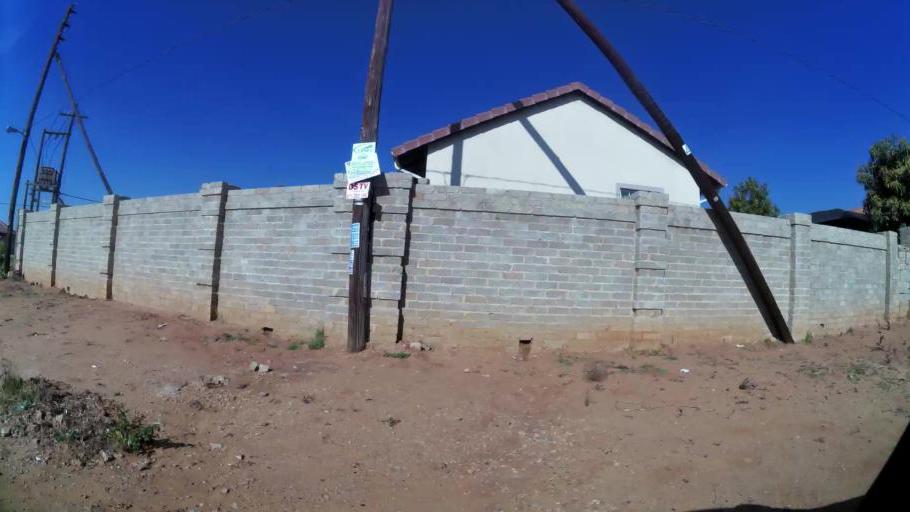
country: ZA
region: Gauteng
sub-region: West Rand District Municipality
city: Muldersdriseloop
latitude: -26.0386
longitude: 27.9268
